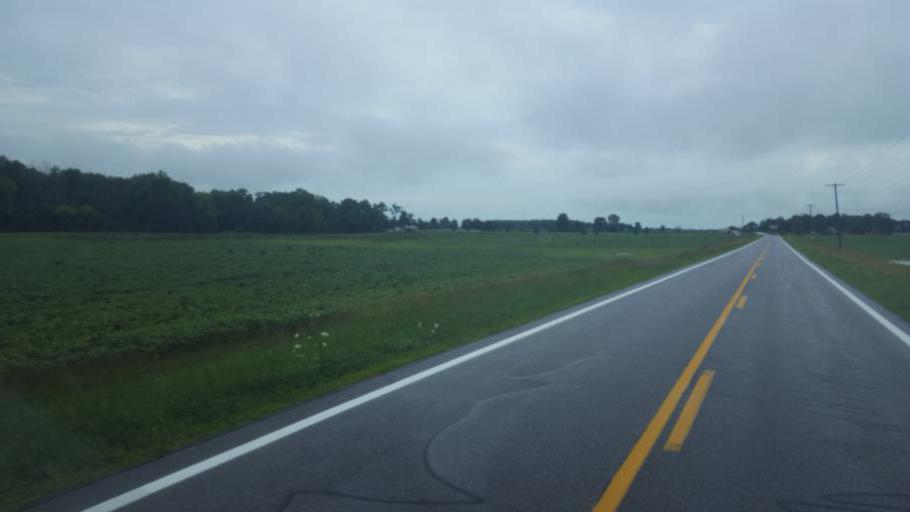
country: US
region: Ohio
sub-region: Union County
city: Richwood
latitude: 40.5020
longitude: -83.2856
